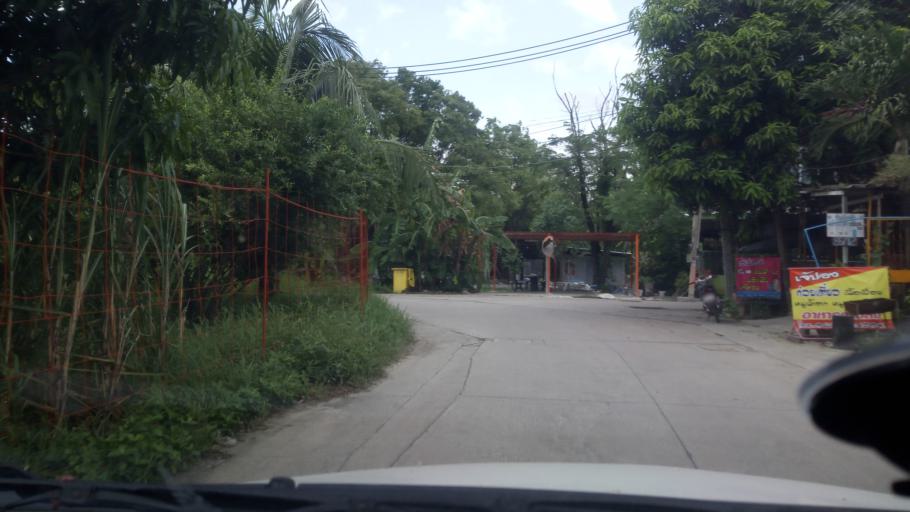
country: TH
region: Chon Buri
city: Phan Thong
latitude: 13.4119
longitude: 101.0522
